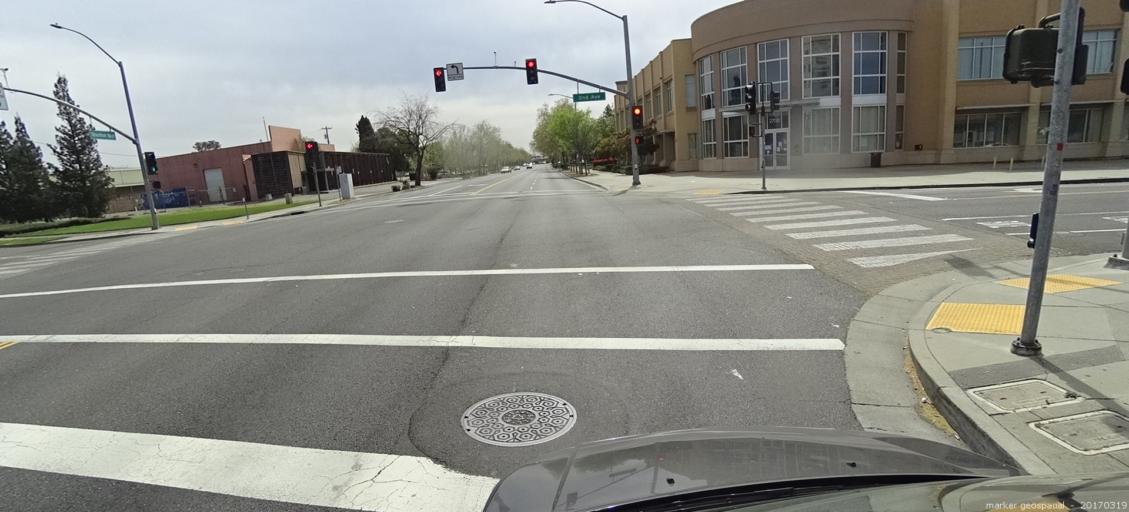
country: US
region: California
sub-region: Sacramento County
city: Sacramento
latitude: 38.5513
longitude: -121.4556
